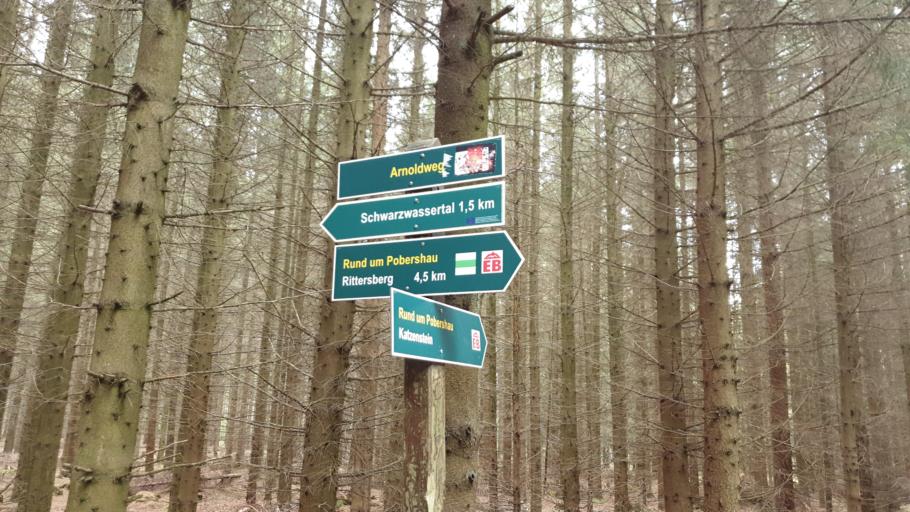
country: DE
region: Saxony
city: Pobershau
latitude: 50.6340
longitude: 13.2359
